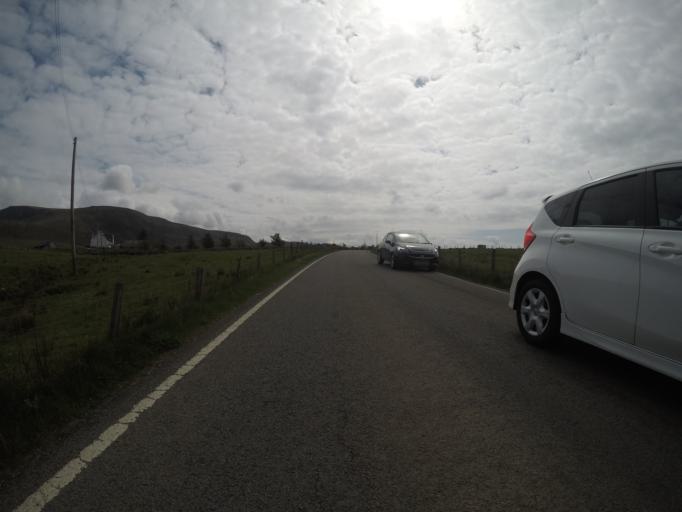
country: GB
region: Scotland
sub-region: Highland
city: Portree
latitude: 57.6420
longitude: -6.3768
